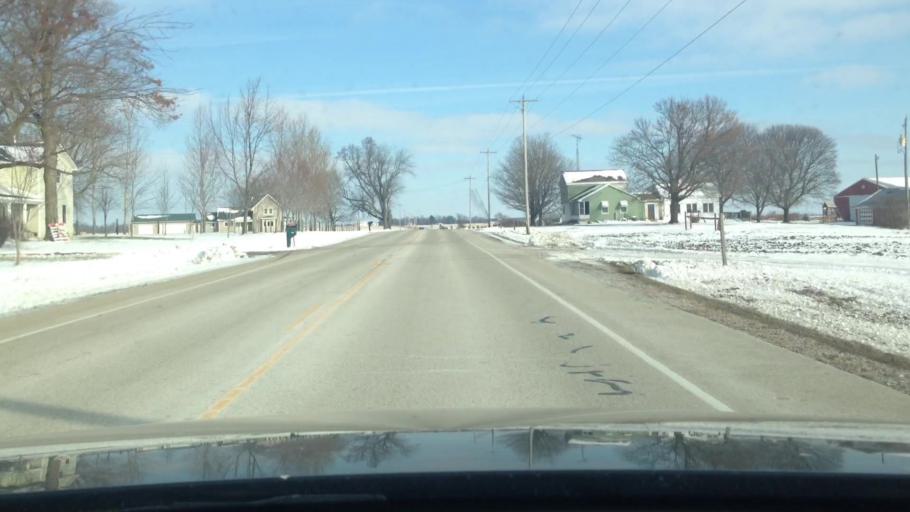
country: US
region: Wisconsin
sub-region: Walworth County
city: Lake Geneva
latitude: 42.6751
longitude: -88.4096
